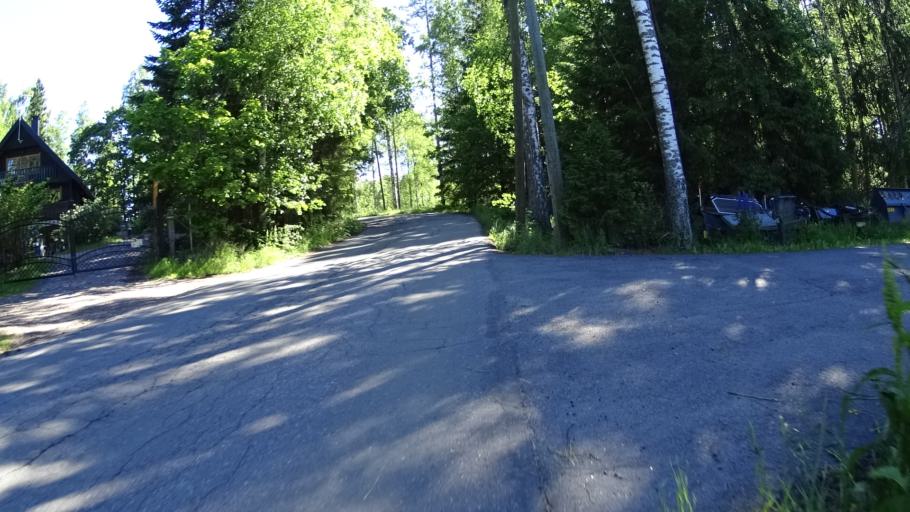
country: FI
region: Uusimaa
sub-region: Helsinki
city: Kilo
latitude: 60.3248
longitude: 24.8094
